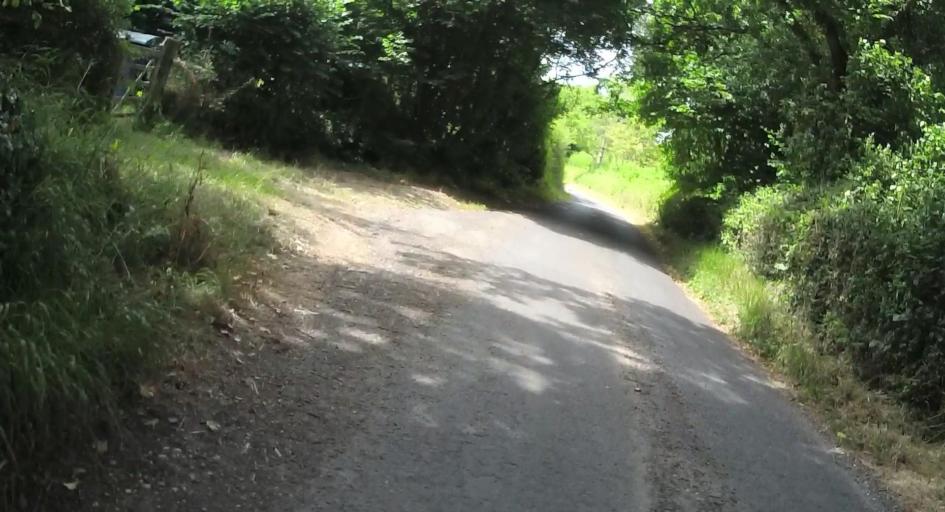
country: GB
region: England
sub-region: Dorset
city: Swanage
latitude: 50.6208
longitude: -1.9864
